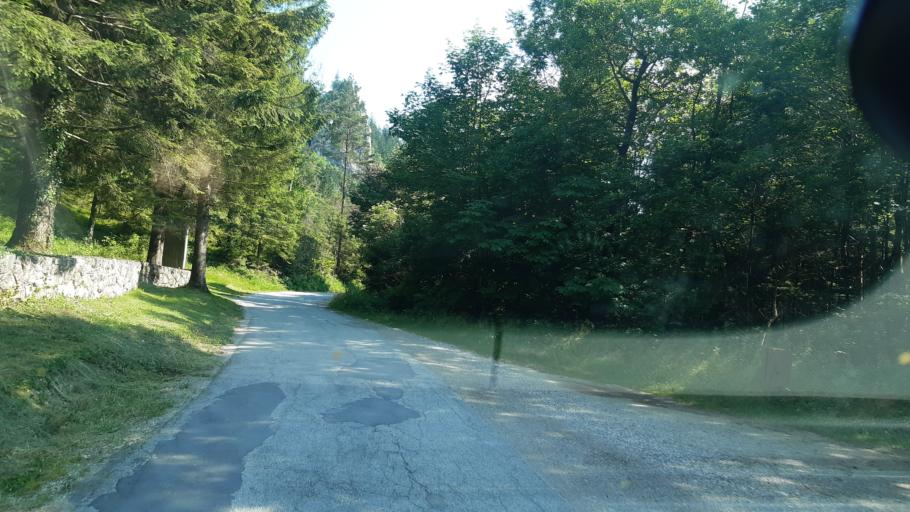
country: SI
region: Radovljica
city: Radovljica
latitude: 46.3842
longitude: 14.2178
